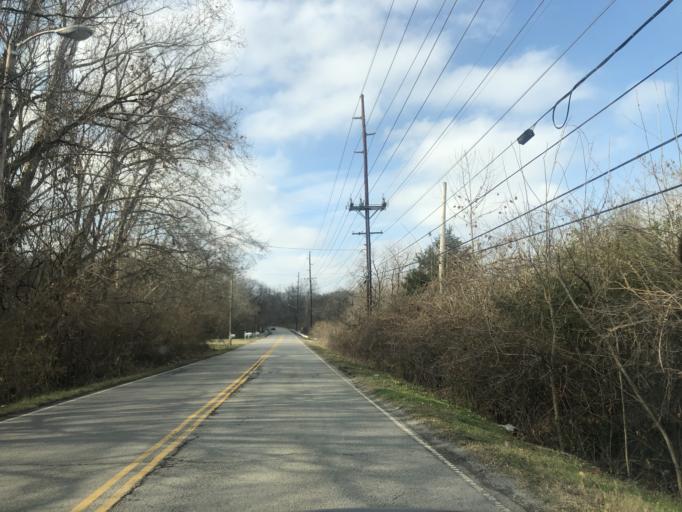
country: US
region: Tennessee
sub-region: Davidson County
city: Oak Hill
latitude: 36.0984
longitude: -86.7118
